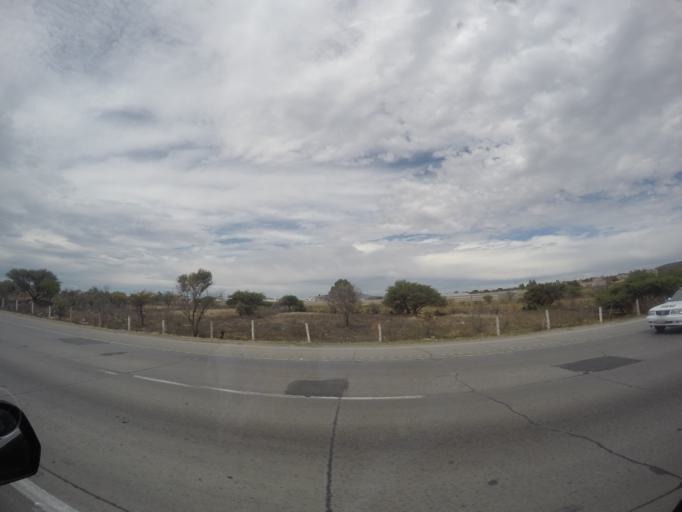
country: MX
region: Queretaro
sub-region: San Juan del Rio
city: Paso de Mata
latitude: 20.3527
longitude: -99.9552
